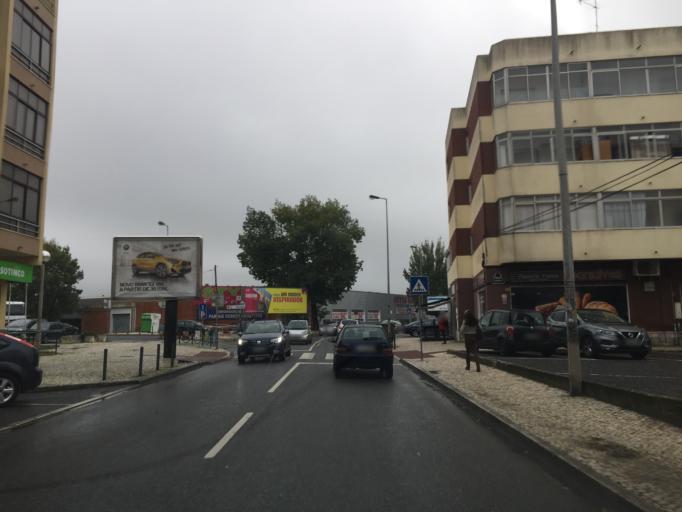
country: PT
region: Lisbon
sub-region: Sintra
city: Rio de Mouro
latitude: 38.7839
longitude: -9.3449
